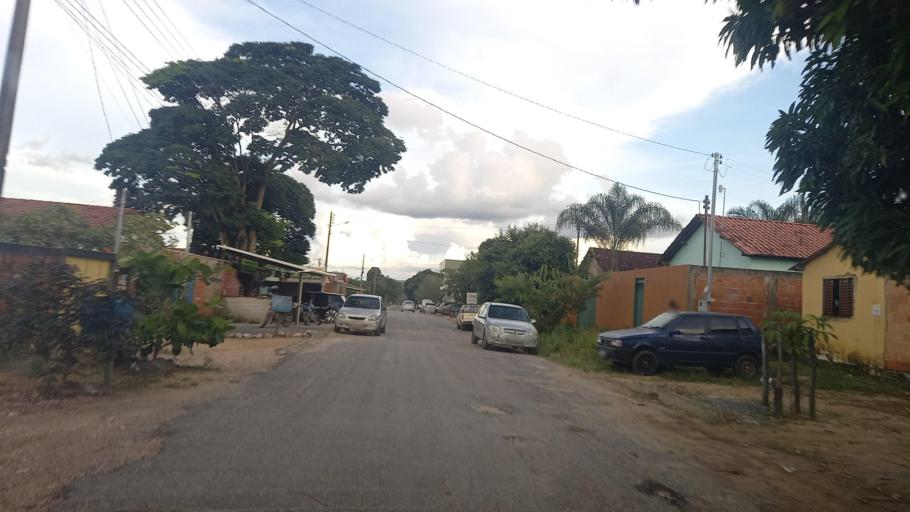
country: BR
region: Goias
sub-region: Cavalcante
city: Cavalcante
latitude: -13.7894
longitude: -47.4584
